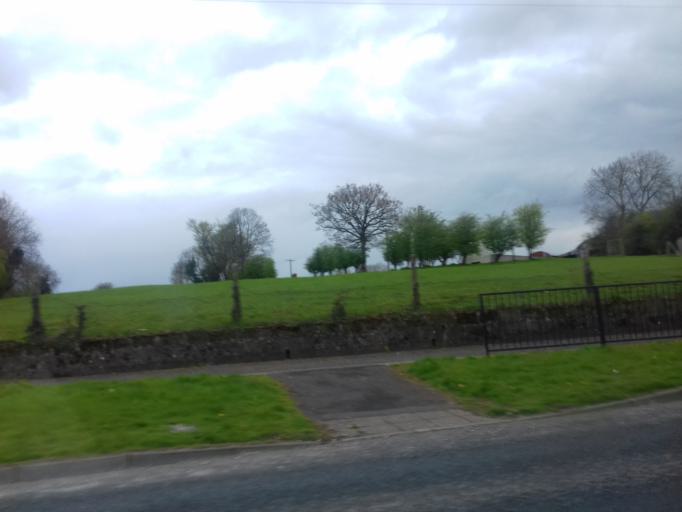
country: IE
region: Ulster
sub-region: An Cabhan
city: Ballyconnell
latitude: 54.1126
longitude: -7.5786
